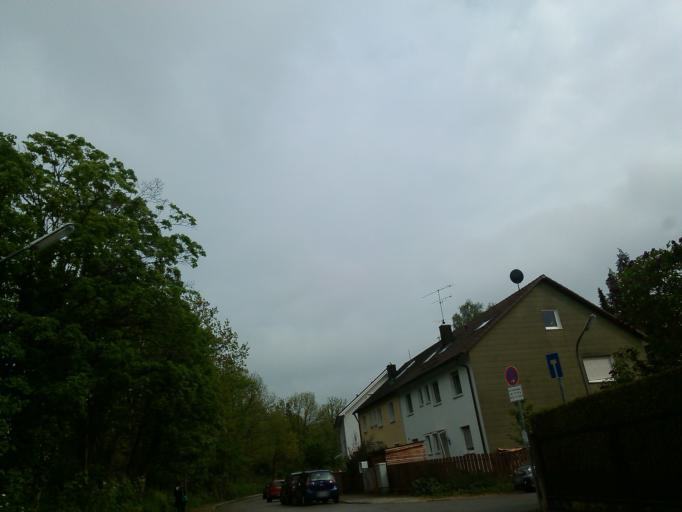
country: DE
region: Bavaria
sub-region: Upper Bavaria
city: Neubiberg
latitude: 48.1086
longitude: 11.6751
